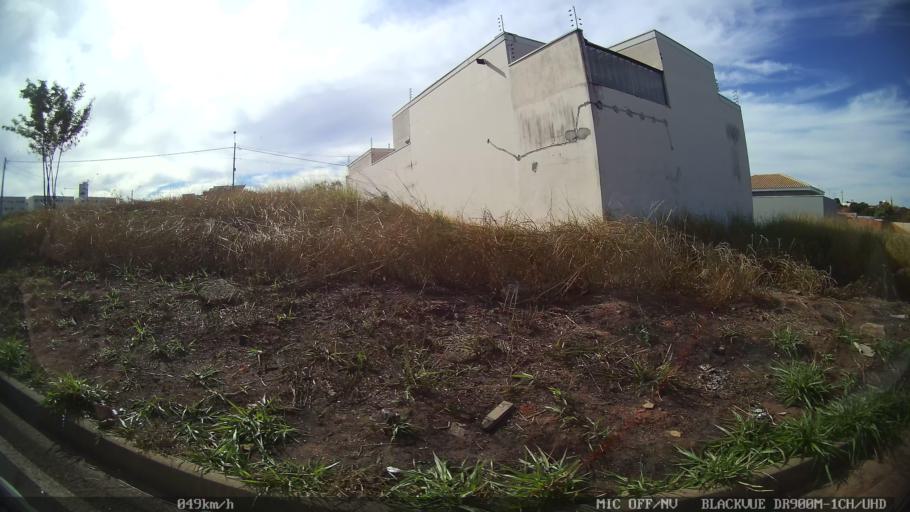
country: BR
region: Sao Paulo
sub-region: Catanduva
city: Catanduva
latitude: -21.1214
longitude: -48.9778
